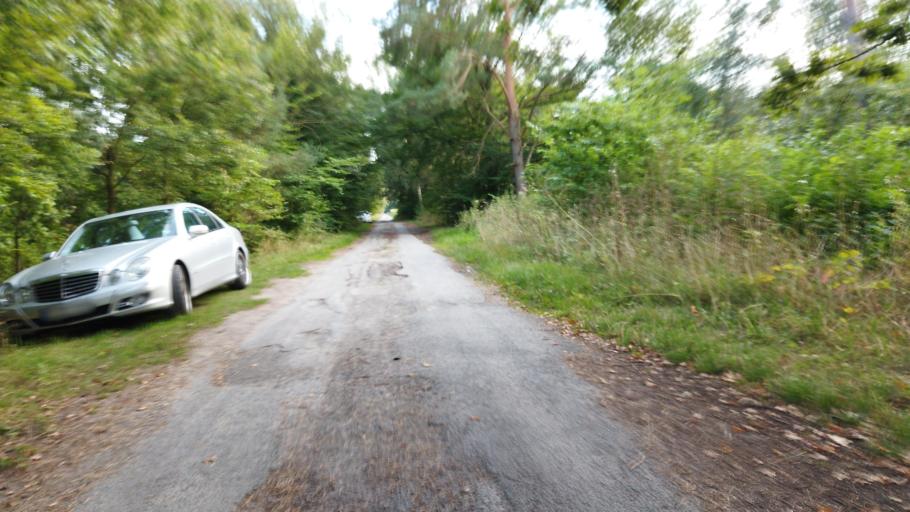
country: DE
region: Lower Saxony
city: Glandorf
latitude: 52.0962
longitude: 8.0360
